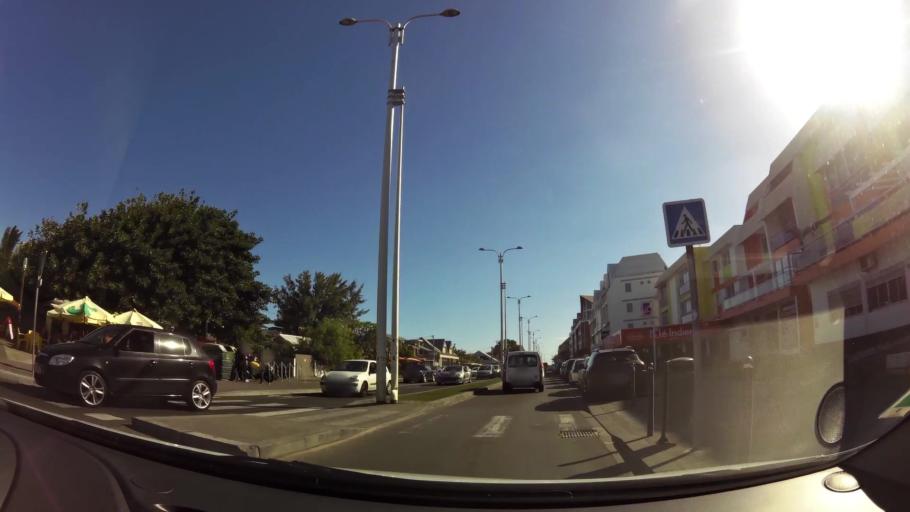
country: RE
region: Reunion
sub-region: Reunion
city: Saint-Pierre
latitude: -21.3435
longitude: 55.4717
